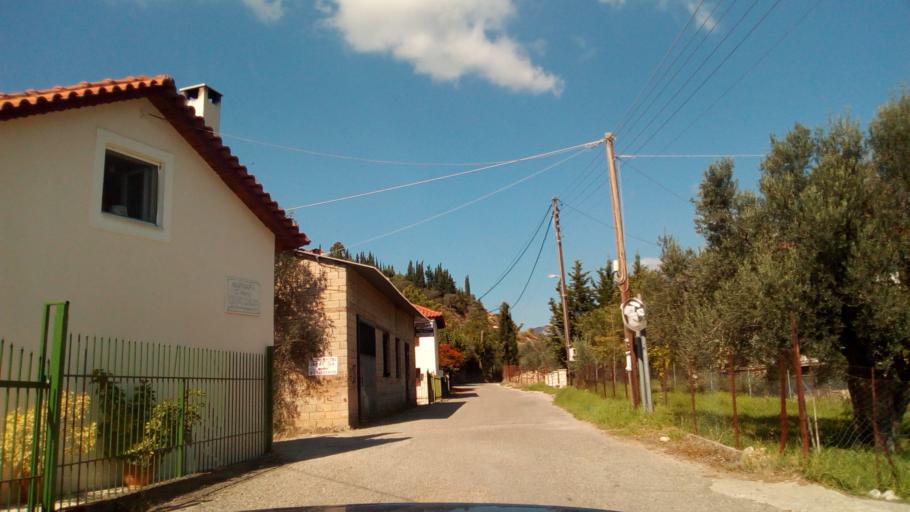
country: GR
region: West Greece
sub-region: Nomos Aitolias kai Akarnanias
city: Nafpaktos
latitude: 38.3892
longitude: 21.7983
